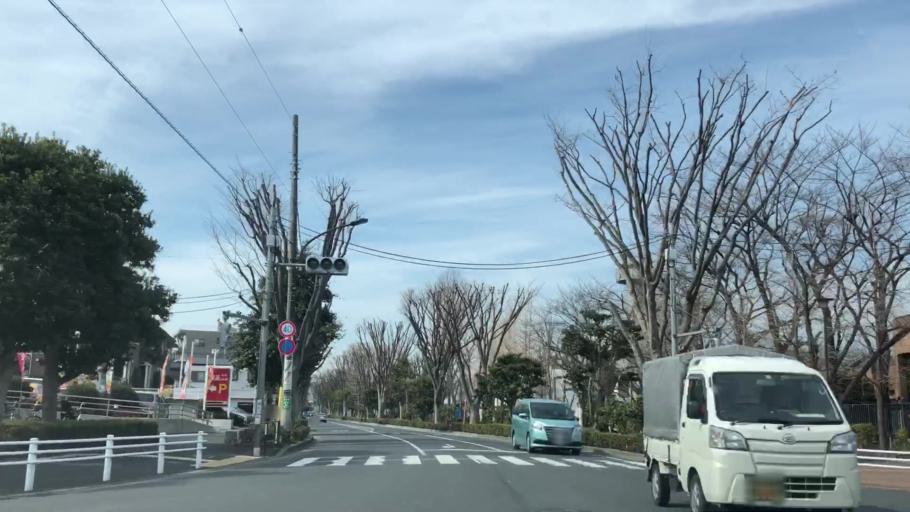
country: JP
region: Saitama
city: Asaka
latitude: 35.7753
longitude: 139.5952
